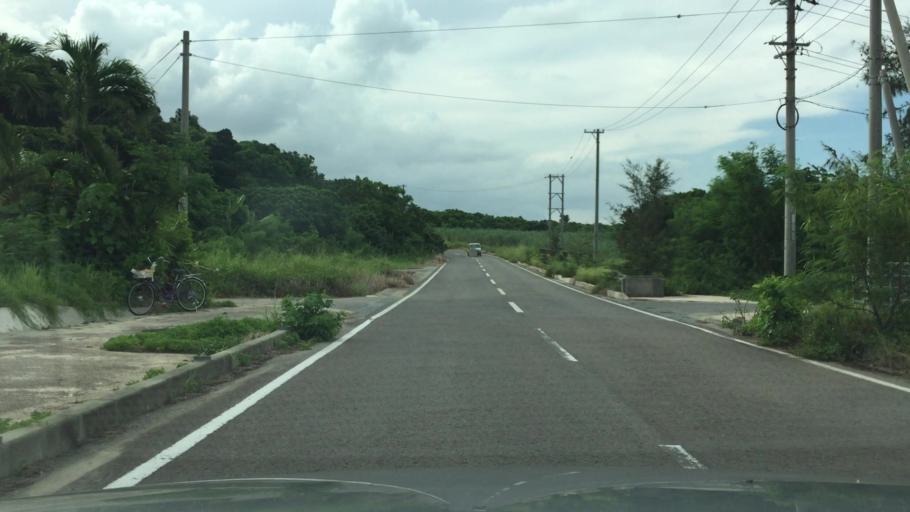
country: JP
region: Okinawa
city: Ishigaki
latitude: 24.4671
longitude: 124.1407
